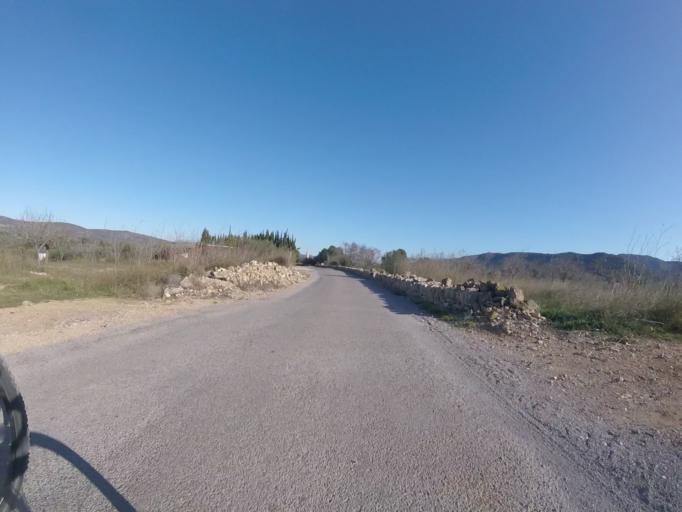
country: ES
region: Valencia
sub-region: Provincia de Castello
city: Alcala de Xivert
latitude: 40.2938
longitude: 0.2185
